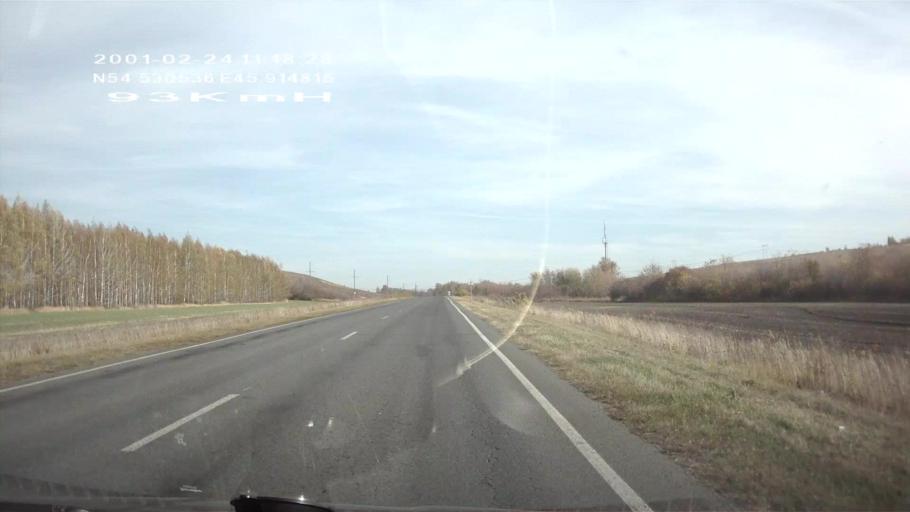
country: RU
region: Mordoviya
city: Atyashevo
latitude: 54.5306
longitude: 45.9149
